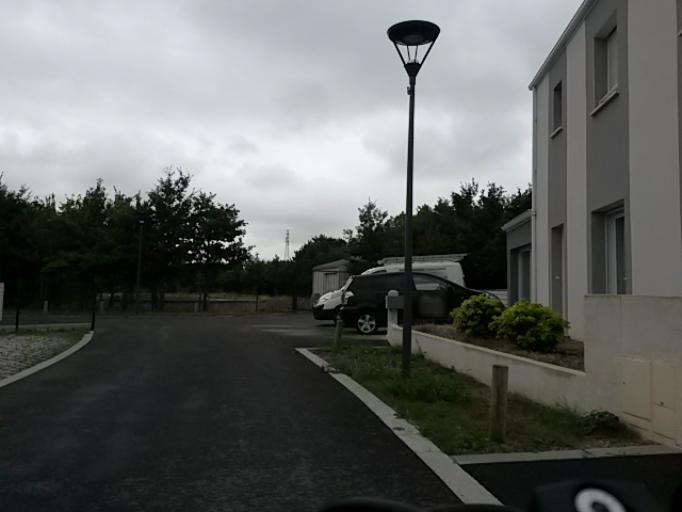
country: FR
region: Poitou-Charentes
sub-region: Departement de la Charente-Maritime
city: Saint-Xandre
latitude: 46.2054
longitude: -1.0910
